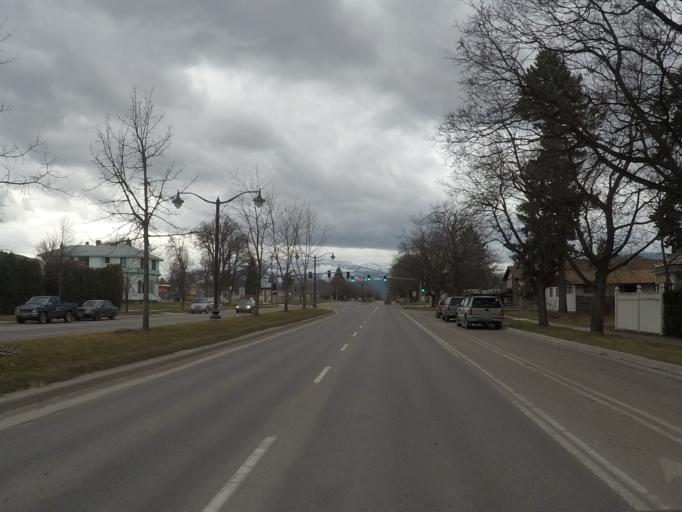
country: US
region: Montana
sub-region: Missoula County
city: Missoula
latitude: 46.8627
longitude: -114.0045
